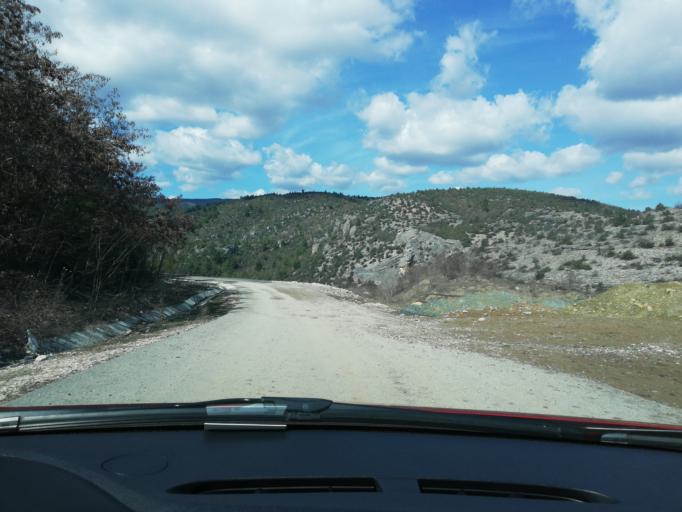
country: TR
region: Kastamonu
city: Igdir
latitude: 41.2288
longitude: 33.0258
